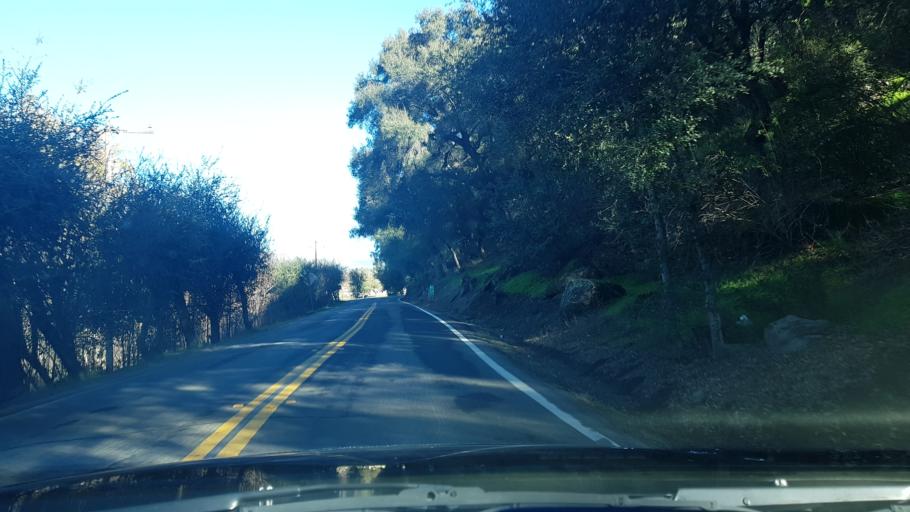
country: US
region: California
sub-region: San Diego County
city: Valley Center
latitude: 33.2058
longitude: -116.9859
